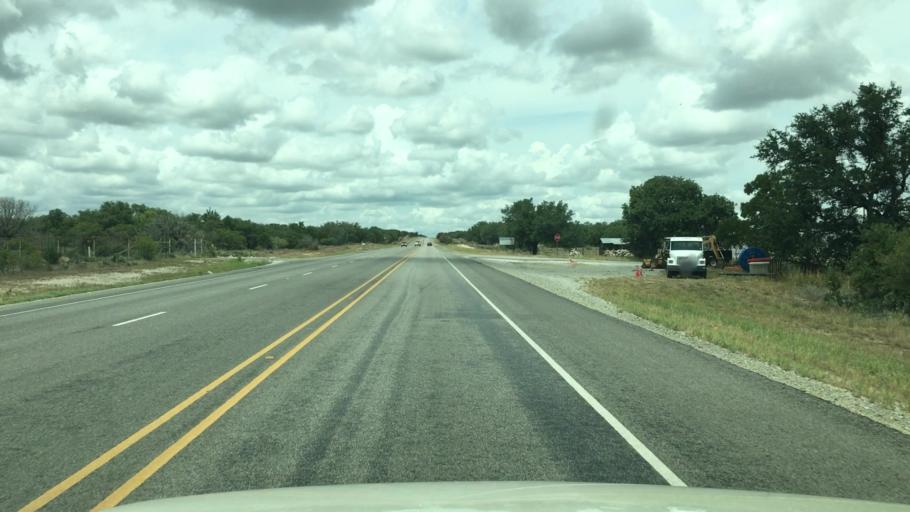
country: US
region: Texas
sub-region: McCulloch County
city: Brady
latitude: 31.0273
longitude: -99.2247
